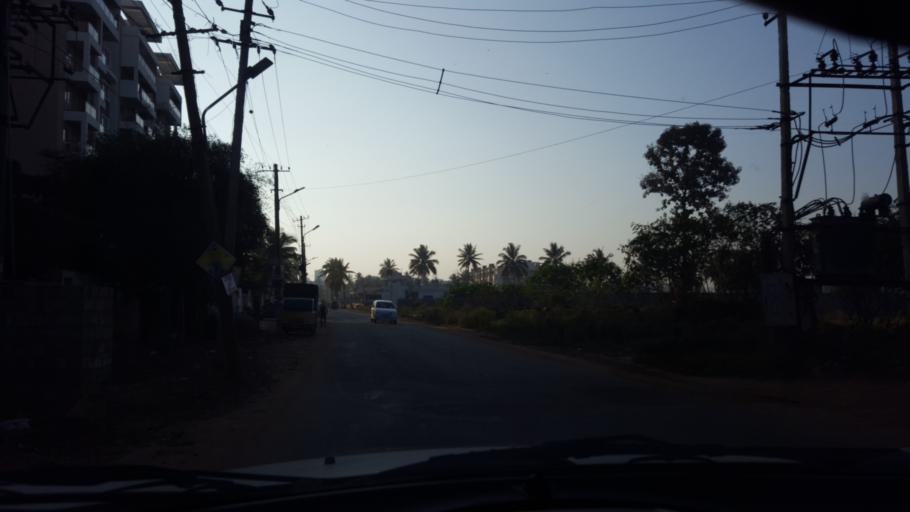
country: IN
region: Karnataka
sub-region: Bangalore Rural
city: Hoskote
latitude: 12.9394
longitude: 77.7364
